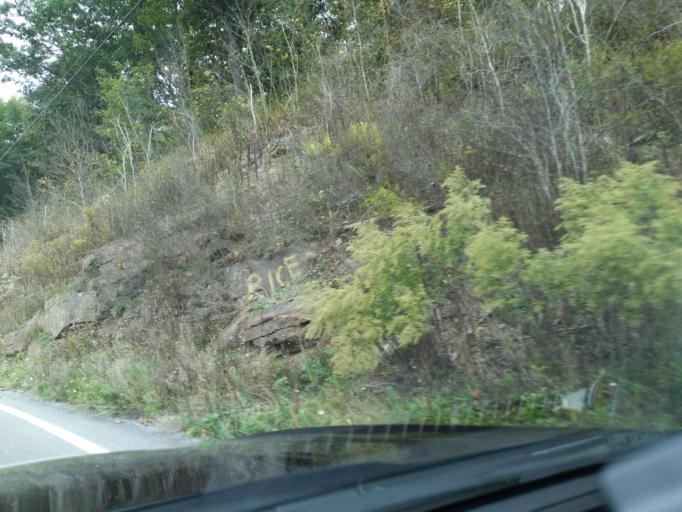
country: US
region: Pennsylvania
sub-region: Blair County
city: Altoona
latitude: 40.4967
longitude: -78.4678
